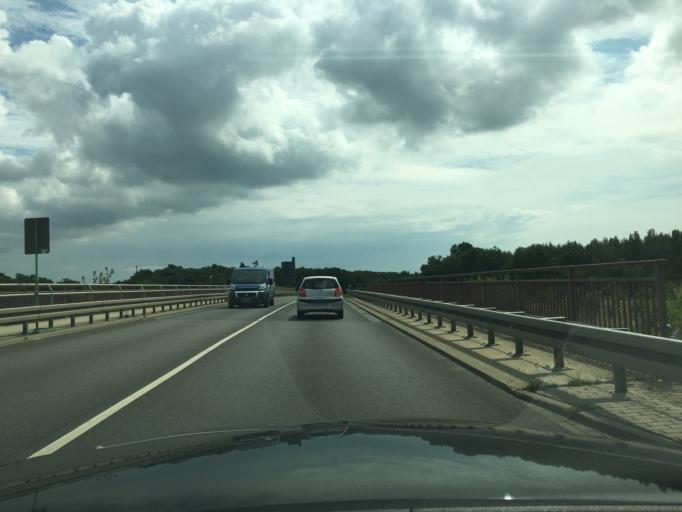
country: DE
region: Saxony-Anhalt
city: Sandersdorf
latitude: 51.6356
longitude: 12.2780
